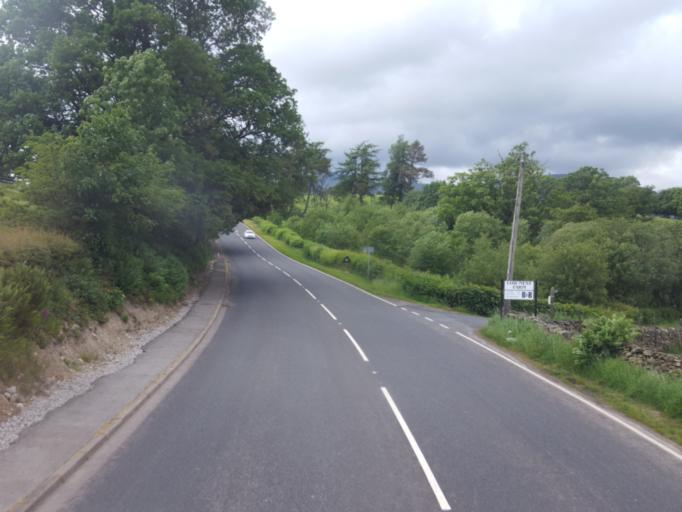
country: GB
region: England
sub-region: Cumbria
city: Keswick
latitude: 54.5924
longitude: -3.1005
